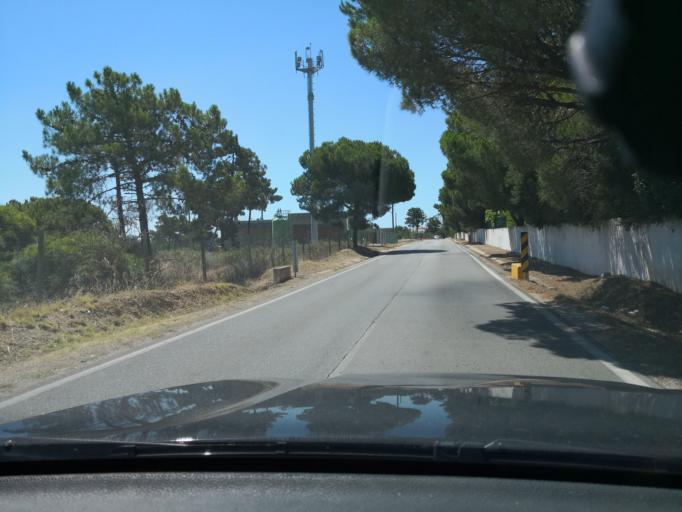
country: PT
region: Faro
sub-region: Loule
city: Vilamoura
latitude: 37.0819
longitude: -8.0997
